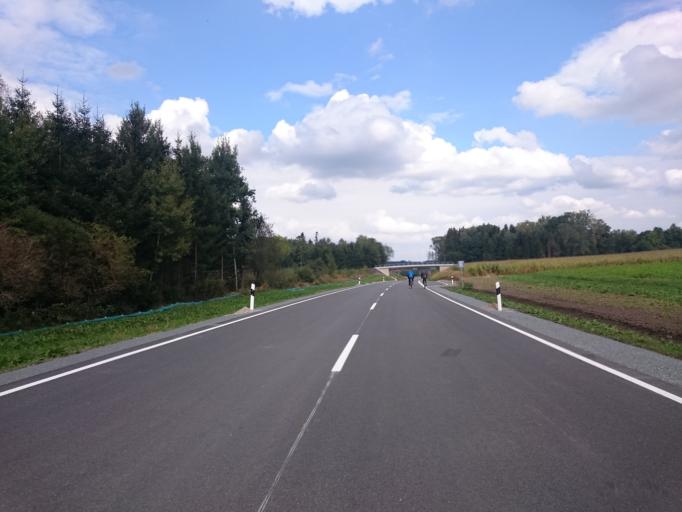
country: DE
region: Bavaria
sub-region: Upper Bavaria
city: Kolbermoor
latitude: 47.8356
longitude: 12.0754
